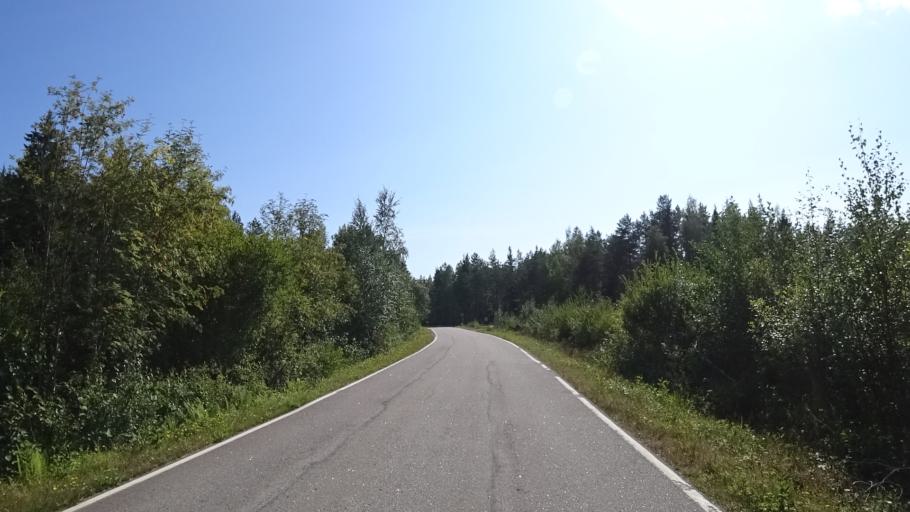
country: FI
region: Kymenlaakso
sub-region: Kotka-Hamina
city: Karhula
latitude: 60.5683
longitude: 26.8989
